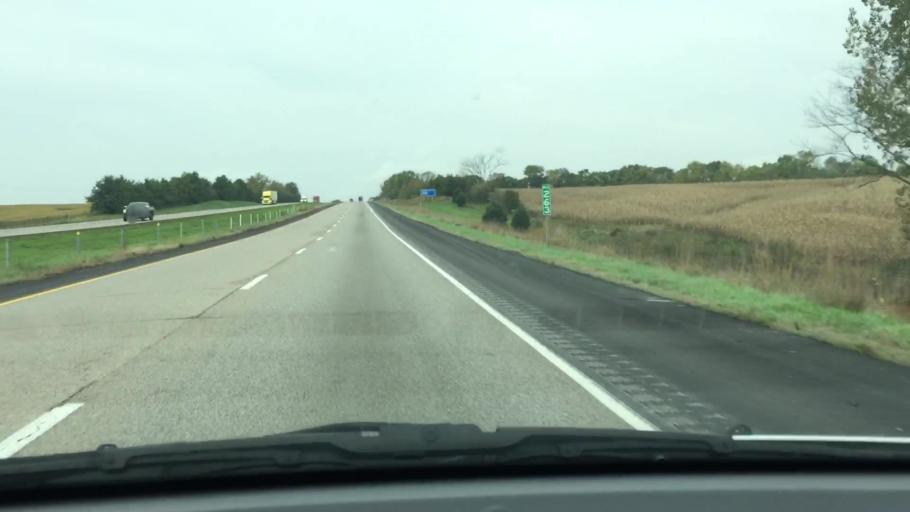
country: US
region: Iowa
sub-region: Muscatine County
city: West Liberty
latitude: 41.6538
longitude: -91.1867
